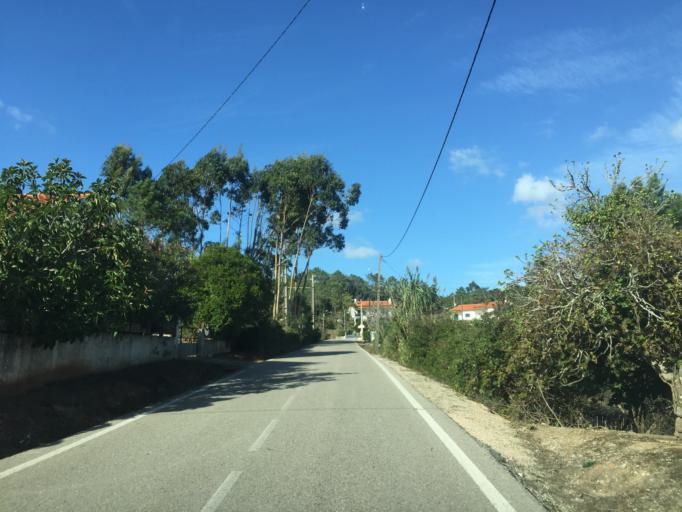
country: PT
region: Coimbra
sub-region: Figueira da Foz
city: Tavarede
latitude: 40.1825
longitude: -8.8378
